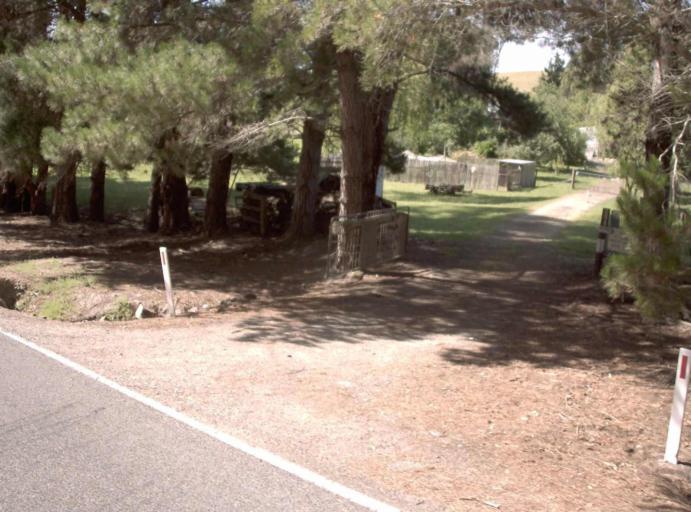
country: AU
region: New South Wales
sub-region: Bombala
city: Bombala
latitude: -37.3798
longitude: 148.6725
